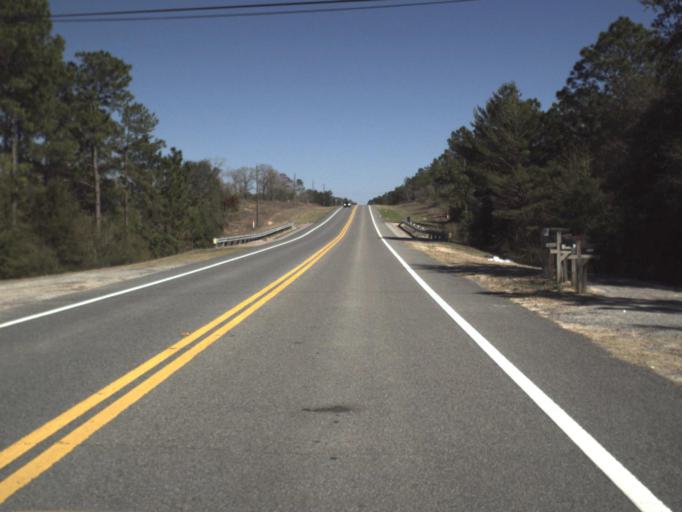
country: US
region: Florida
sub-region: Bay County
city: Youngstown
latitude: 30.4361
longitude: -85.4713
